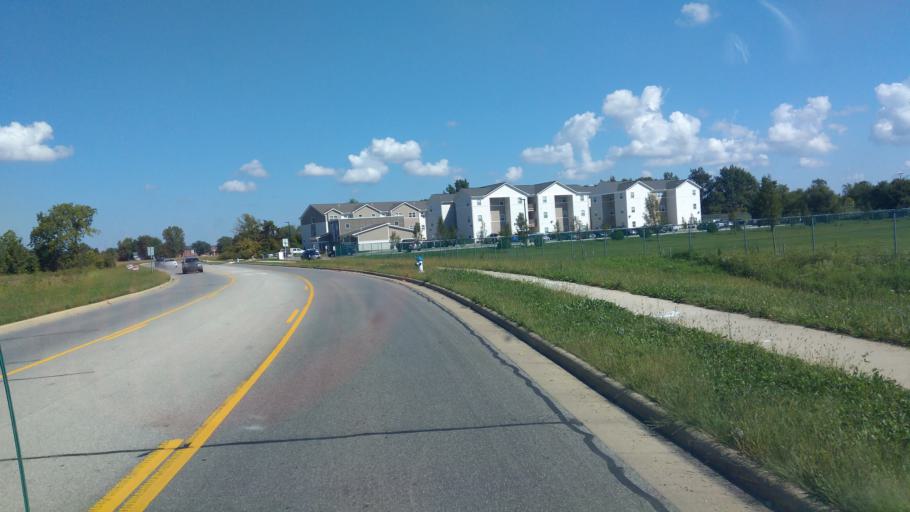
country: US
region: Ohio
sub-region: Marion County
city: Marion
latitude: 40.5835
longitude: -83.0915
